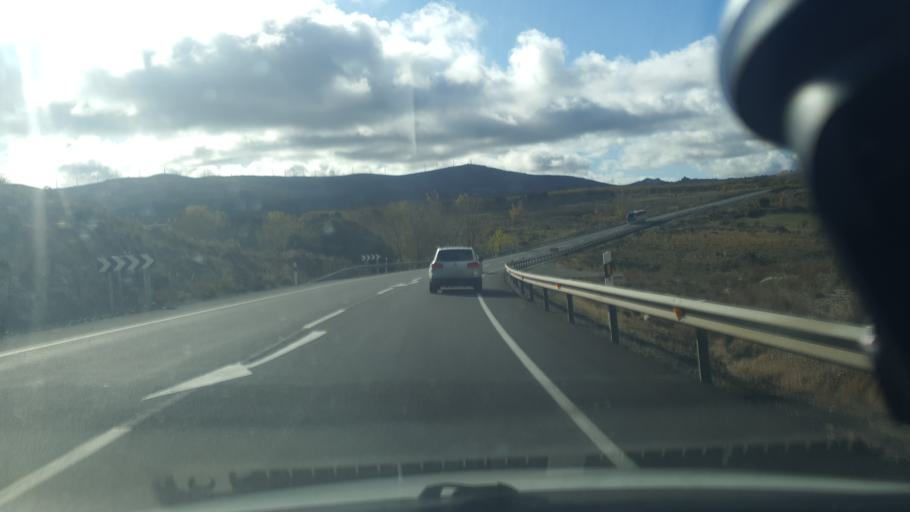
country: ES
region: Castille and Leon
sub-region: Provincia de Segovia
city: Villacastin
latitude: 40.7603
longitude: -4.4362
